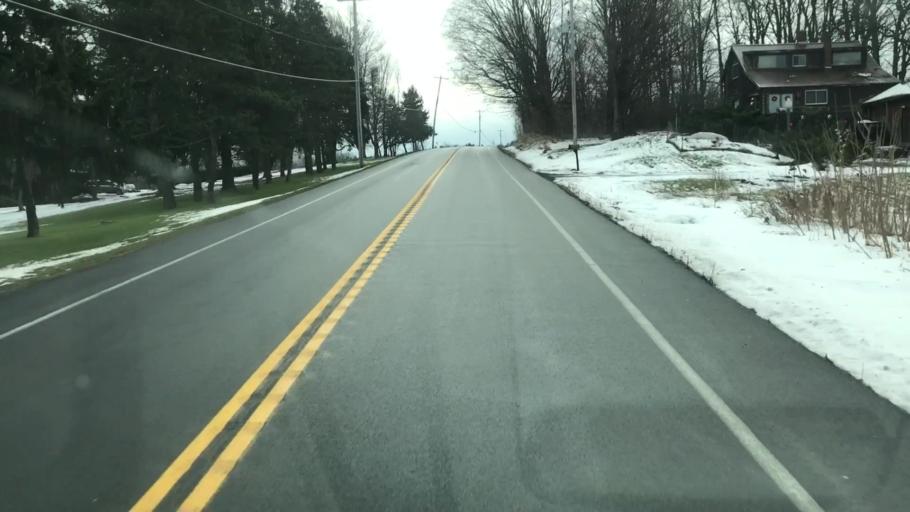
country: US
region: New York
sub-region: Onondaga County
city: Skaneateles
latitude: 42.8466
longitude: -76.3890
